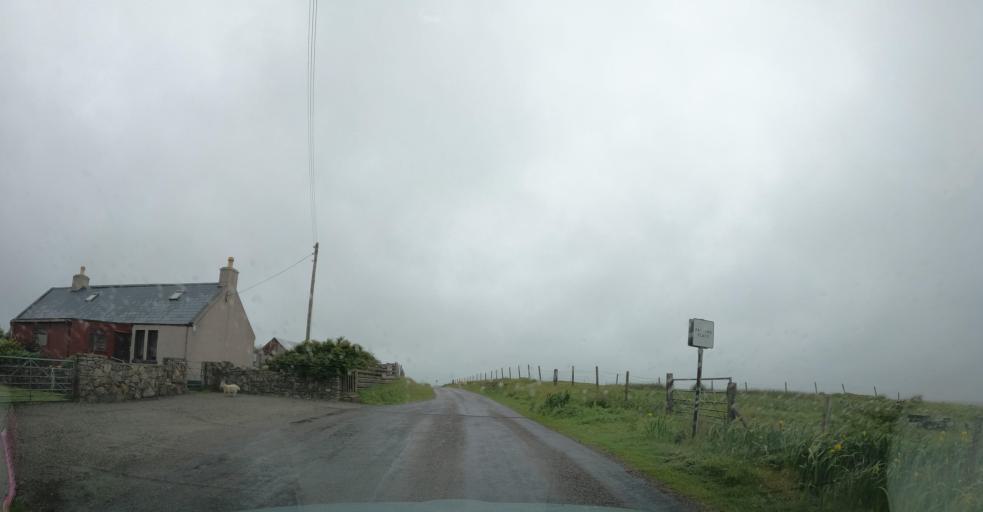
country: GB
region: Scotland
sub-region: Eilean Siar
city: Benbecula
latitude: 57.4996
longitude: -7.2562
